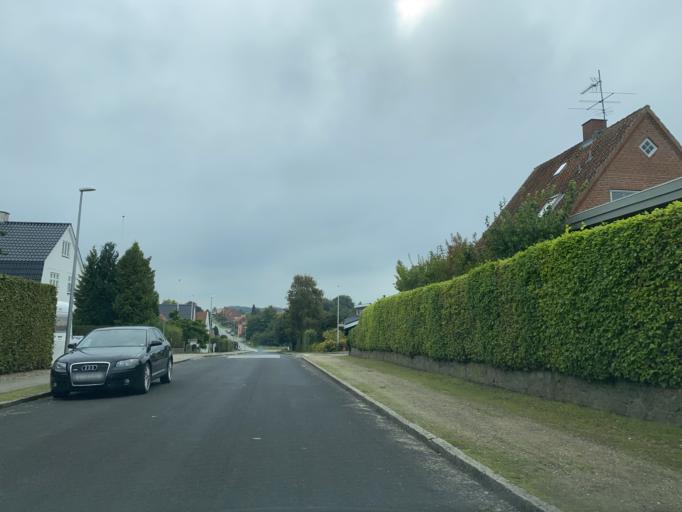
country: DK
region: South Denmark
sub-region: Haderslev Kommune
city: Haderslev
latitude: 55.2422
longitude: 9.4955
